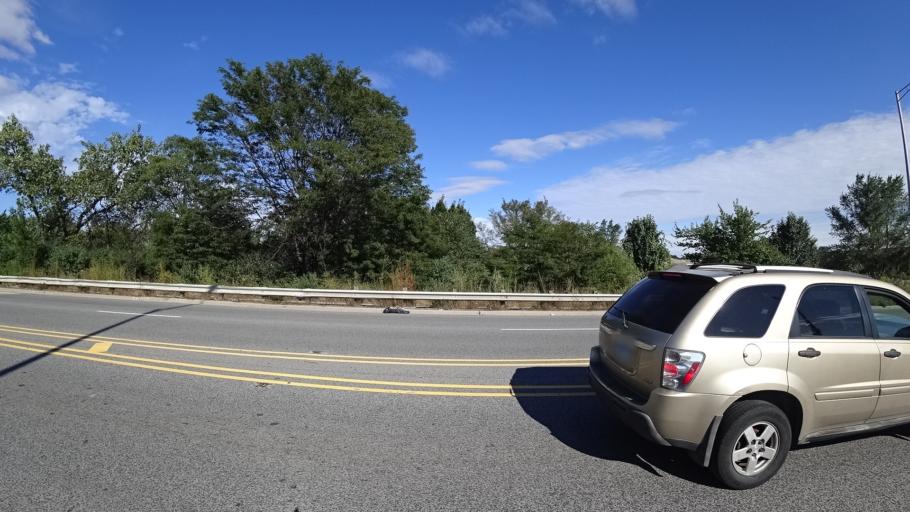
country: US
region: Illinois
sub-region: Cook County
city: Alsip
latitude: 41.6546
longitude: -87.7384
